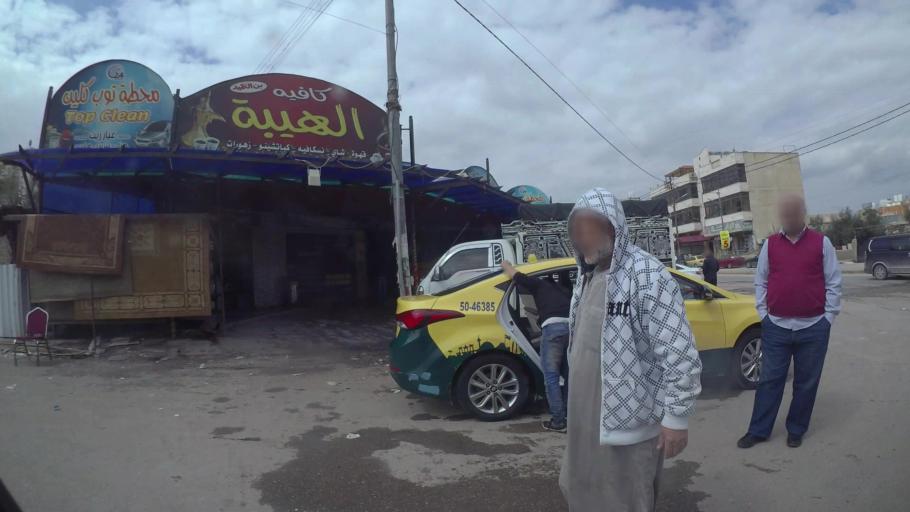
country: JO
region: Amman
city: Al Jubayhah
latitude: 32.0582
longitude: 35.8286
